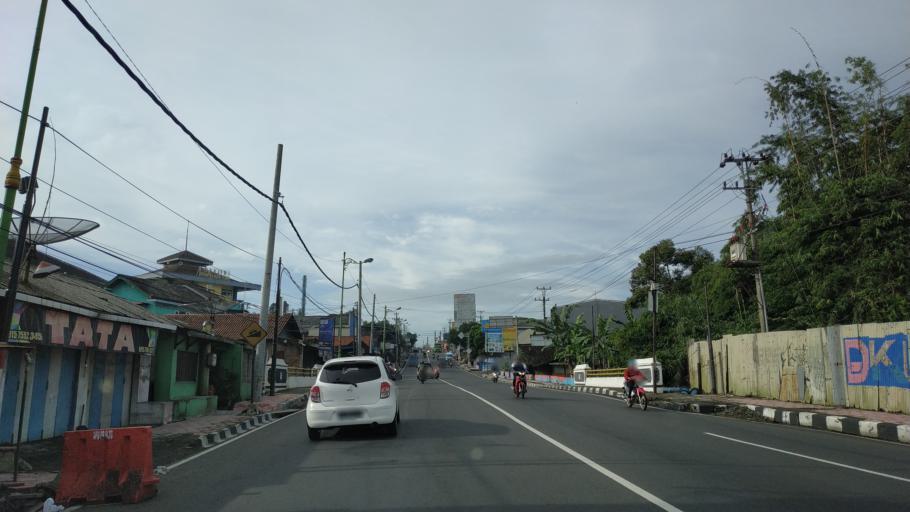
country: ID
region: Central Java
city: Salatiga
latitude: -7.3432
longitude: 110.5102
